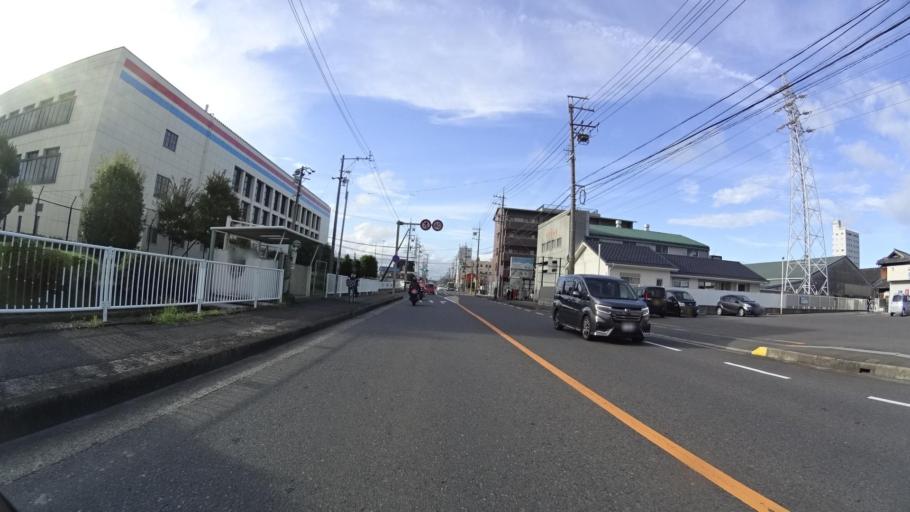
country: JP
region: Mie
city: Suzuka
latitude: 34.8669
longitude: 136.5332
